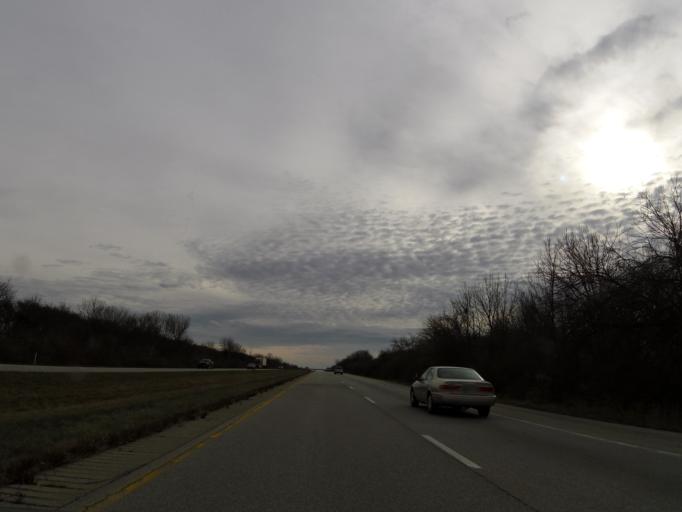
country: US
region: Indiana
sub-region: Montgomery County
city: Crawfordsville
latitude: 39.9972
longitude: -86.7250
